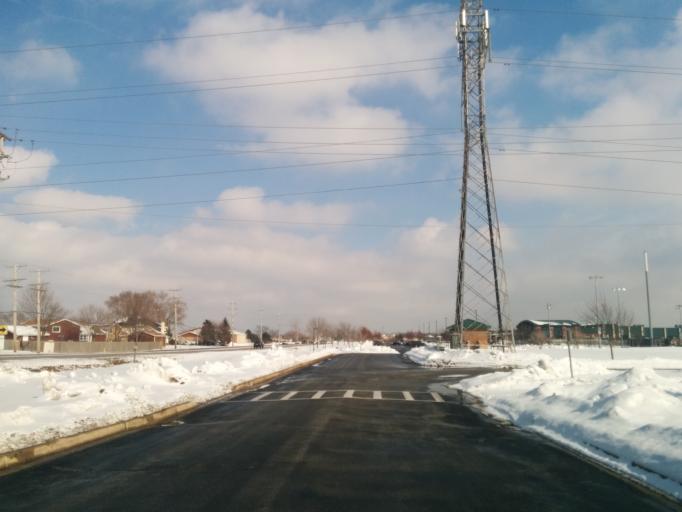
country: US
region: Illinois
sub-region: Cook County
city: Orland Hills
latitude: 41.5798
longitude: -87.8189
